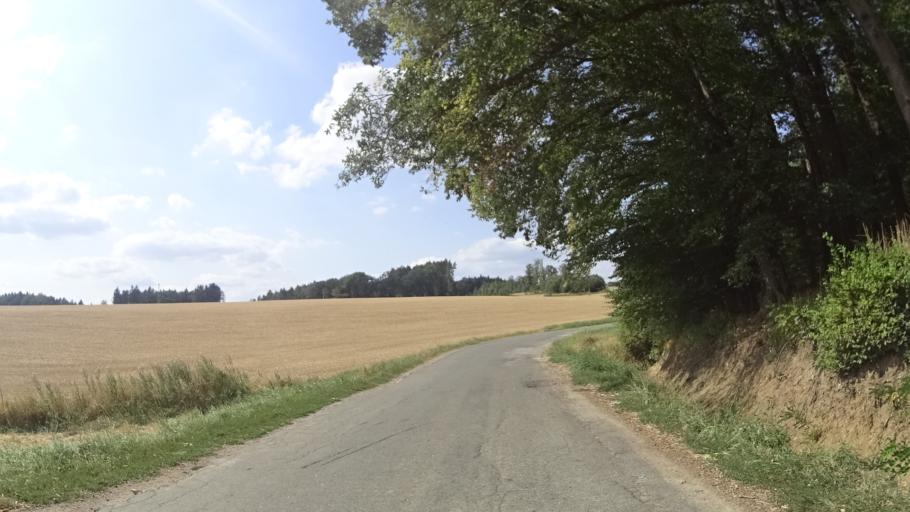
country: CZ
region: Kralovehradecky
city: Liban
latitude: 50.4260
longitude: 15.2607
